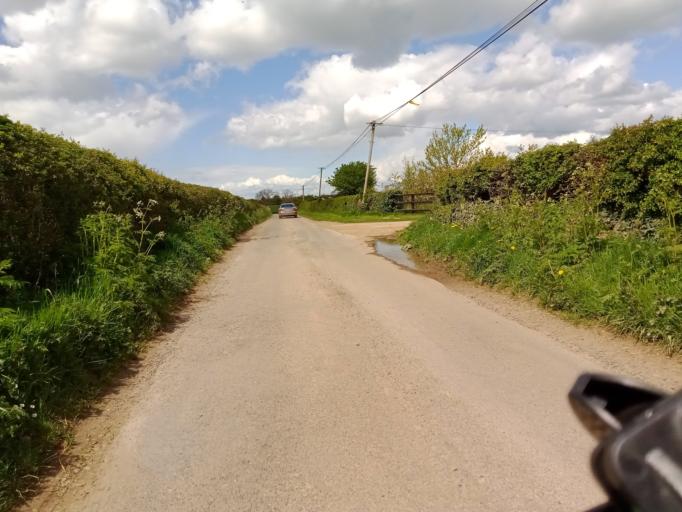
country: IE
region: Leinster
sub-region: Kilkenny
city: Thomastown
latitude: 52.5920
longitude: -7.1482
